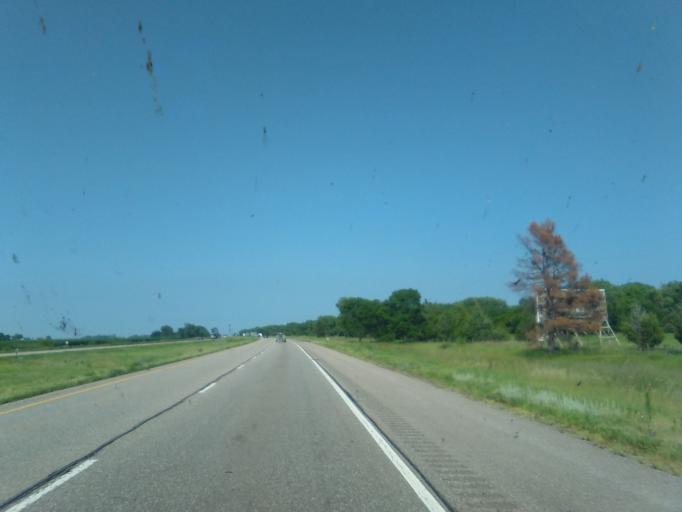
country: US
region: Nebraska
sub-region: Hall County
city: Wood River
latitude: 40.7708
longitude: -98.5603
